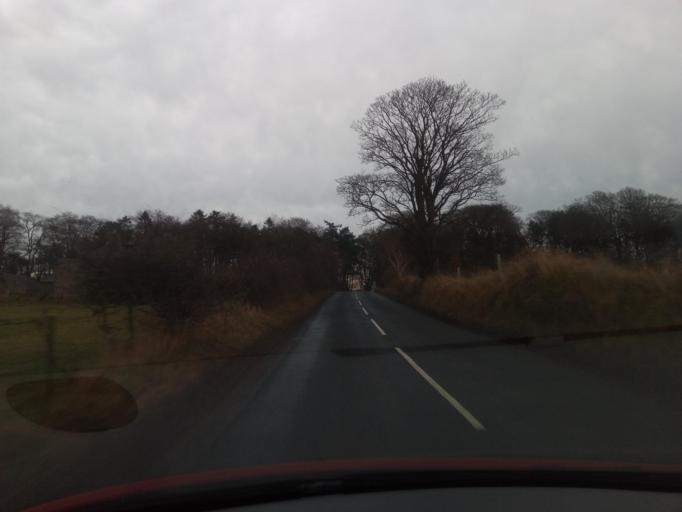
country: GB
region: England
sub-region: Northumberland
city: Whittingham
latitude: 55.4713
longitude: -1.8437
